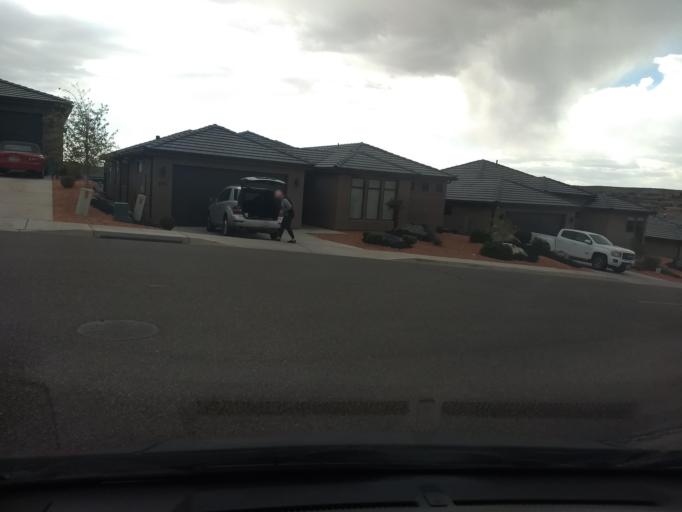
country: US
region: Utah
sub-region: Washington County
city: Washington
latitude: 37.1598
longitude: -113.5251
